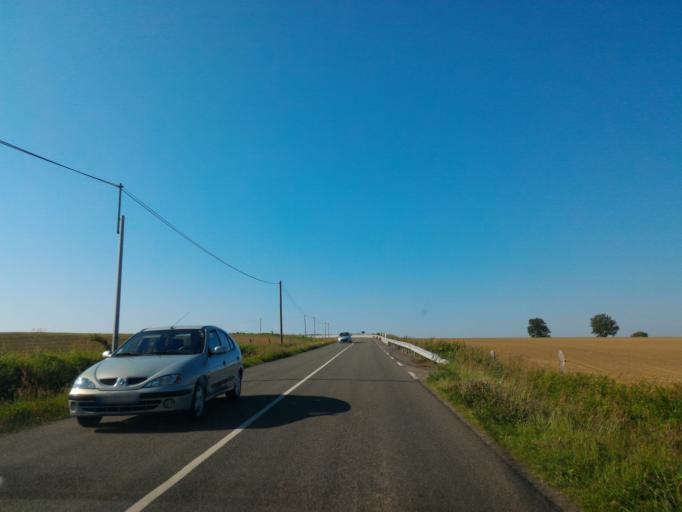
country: FR
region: Brittany
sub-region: Departement d'Ille-et-Vilaine
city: Luitre
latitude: 48.2558
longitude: -1.1274
